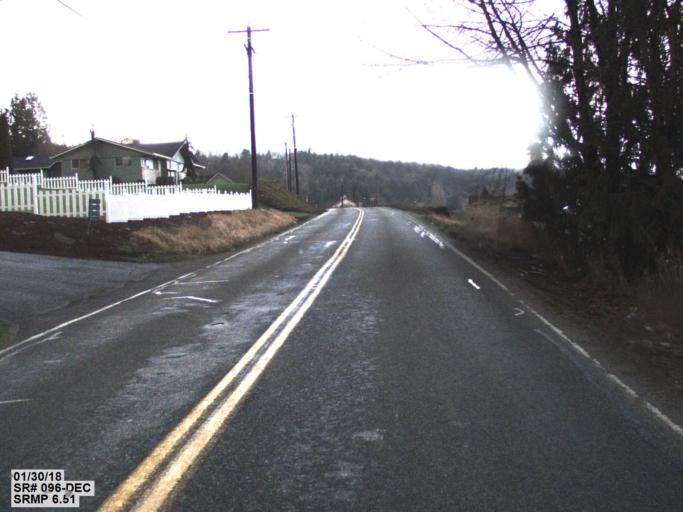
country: US
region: Washington
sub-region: Snohomish County
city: Cathcart
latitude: 47.8794
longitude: -122.1145
